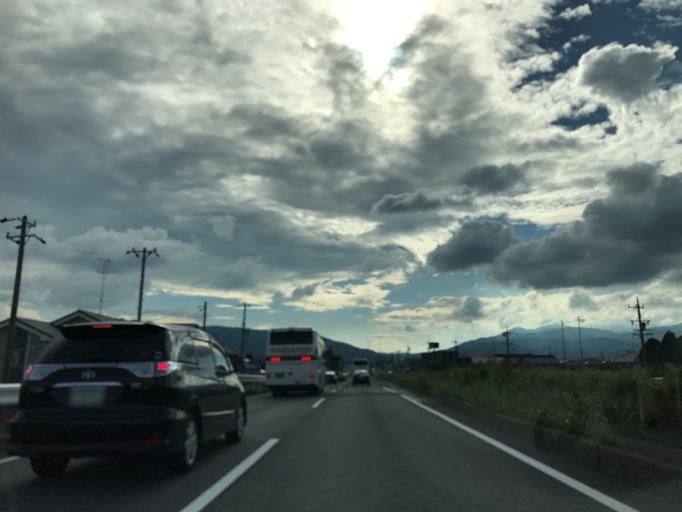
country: JP
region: Gifu
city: Tarui
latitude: 35.3680
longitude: 136.5693
